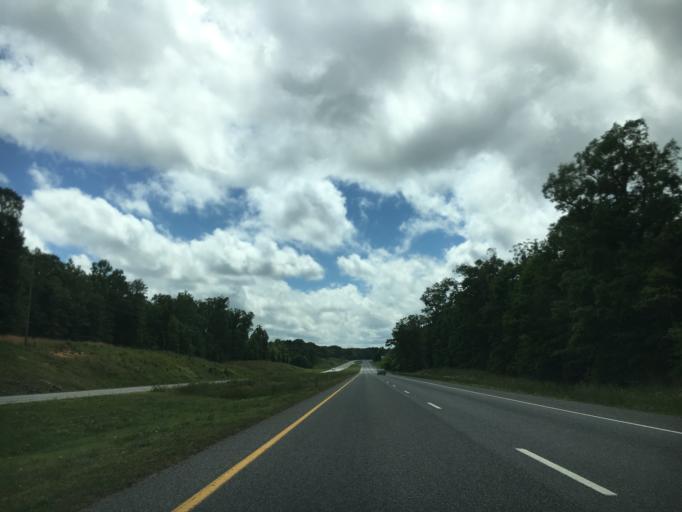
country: US
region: Virginia
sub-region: Mecklenburg County
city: Clarksville
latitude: 36.6436
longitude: -78.5091
